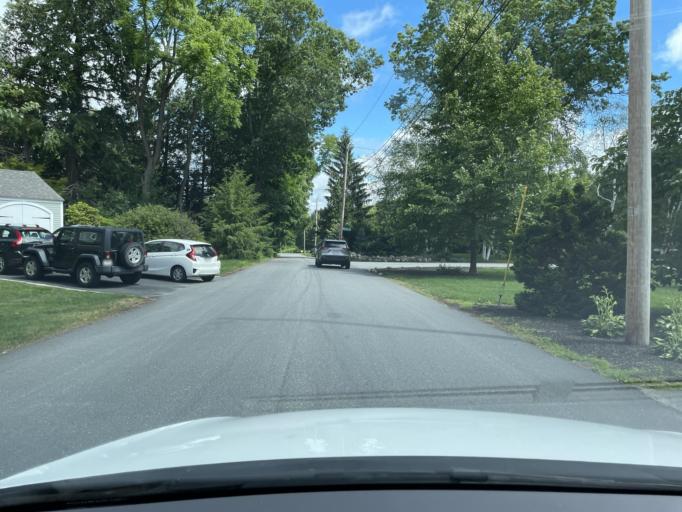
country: US
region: Massachusetts
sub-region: Essex County
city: Andover
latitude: 42.6441
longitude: -71.1242
